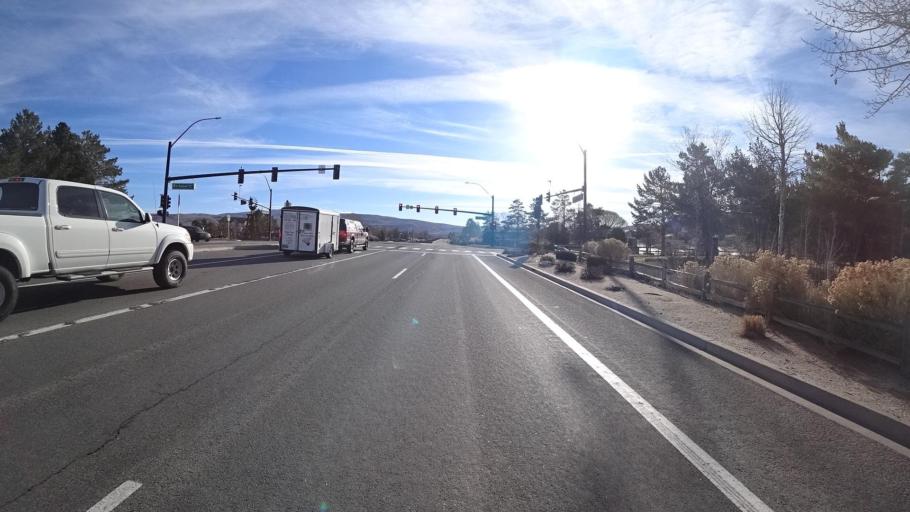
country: US
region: Nevada
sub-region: Washoe County
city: Spanish Springs
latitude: 39.6070
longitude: -119.6867
